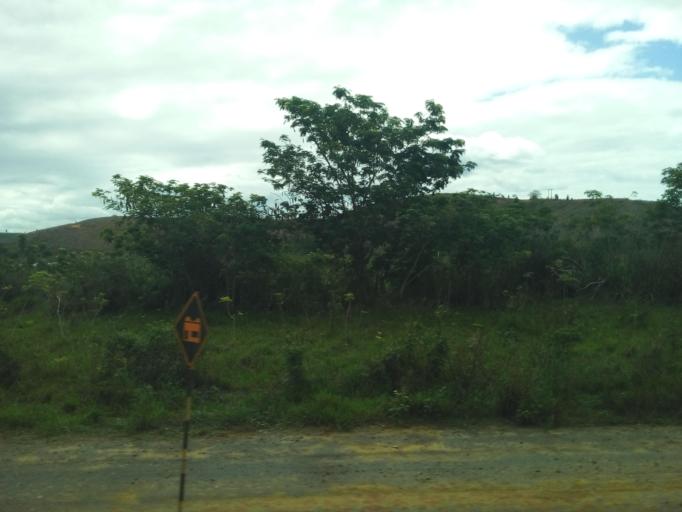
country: BR
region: Minas Gerais
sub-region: Governador Valadares
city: Governador Valadares
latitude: -19.0865
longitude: -42.1624
